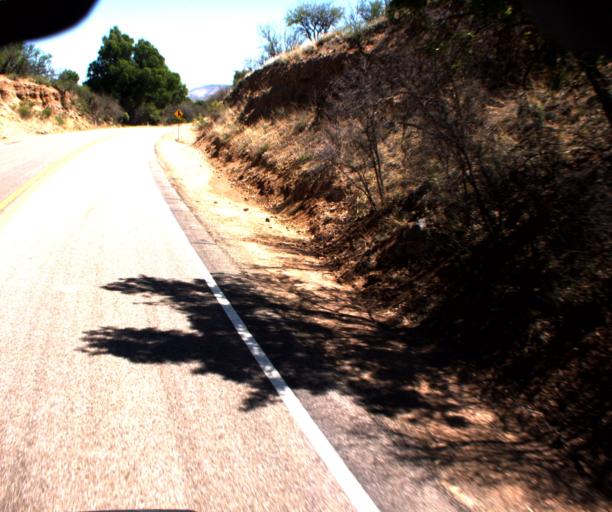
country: US
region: Arizona
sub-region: Santa Cruz County
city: Rio Rico
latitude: 31.5331
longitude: -110.7643
